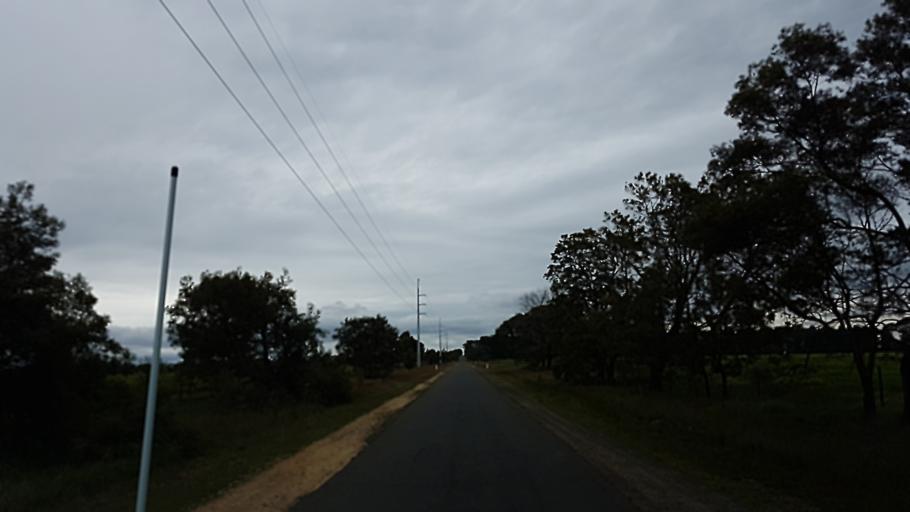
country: AU
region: Victoria
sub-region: Ballarat North
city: Mount Clear
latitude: -37.7809
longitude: 143.9803
